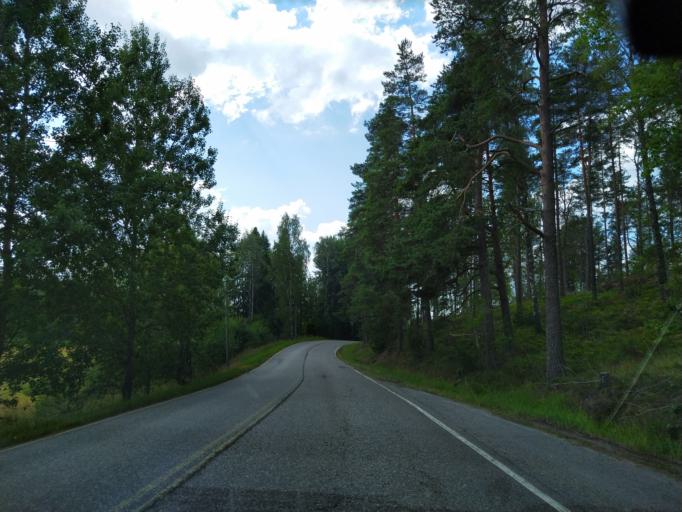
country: FI
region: Uusimaa
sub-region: Helsinki
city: Kirkkonummi
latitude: 60.0838
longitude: 24.4995
